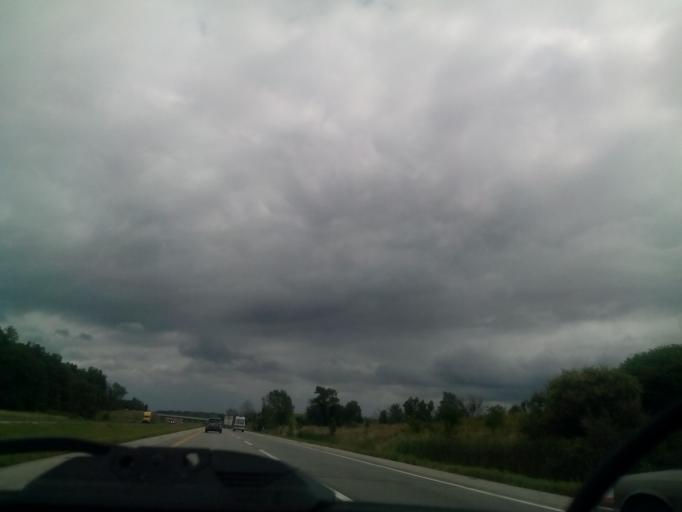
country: US
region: Indiana
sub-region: Steuben County
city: Fremont
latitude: 41.6782
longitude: -84.8745
